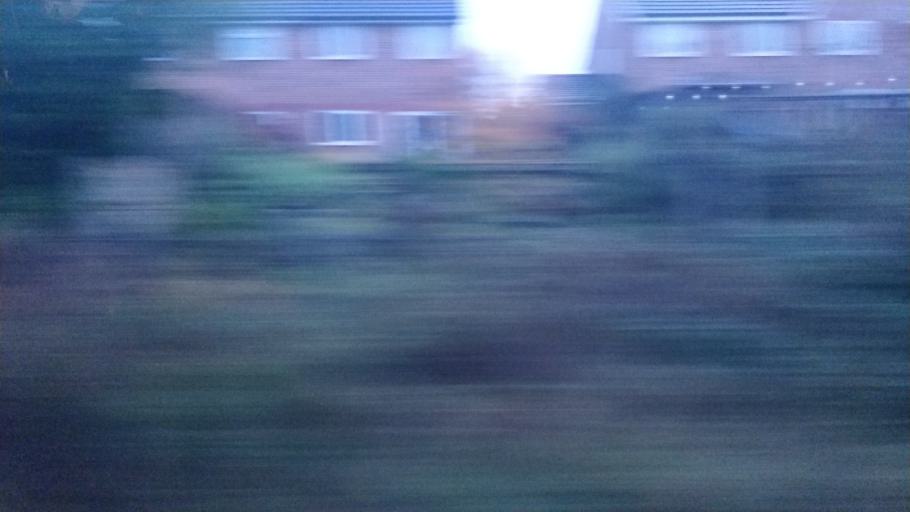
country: GB
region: England
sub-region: Borough of Bolton
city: Westhoughton
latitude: 53.5421
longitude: -2.5298
